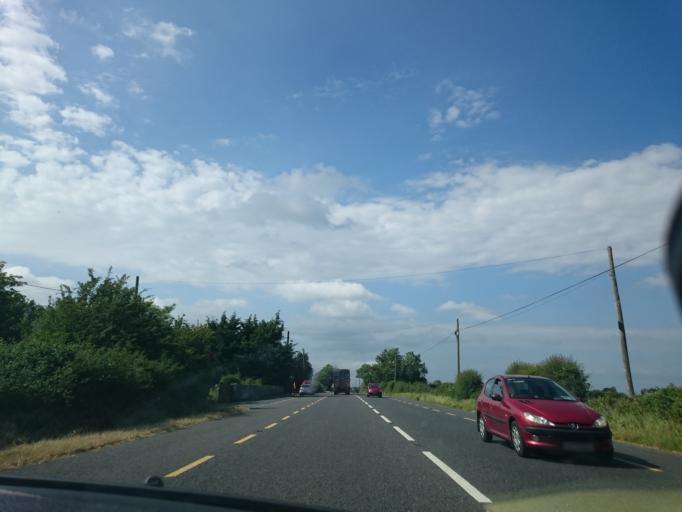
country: IE
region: Leinster
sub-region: Kilkenny
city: Kilkenny
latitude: 52.6121
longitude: -7.2452
